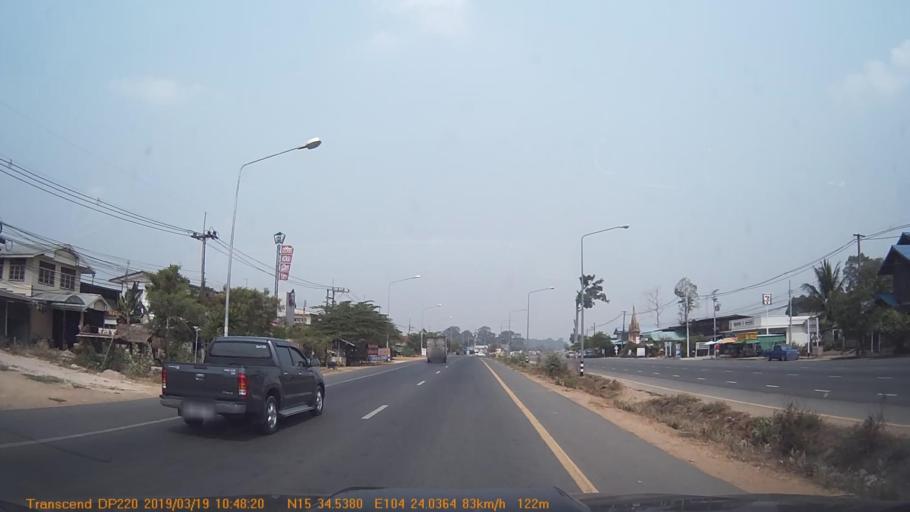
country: TH
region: Yasothon
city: Kham Khuean Kaeo
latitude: 15.5759
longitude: 104.4004
